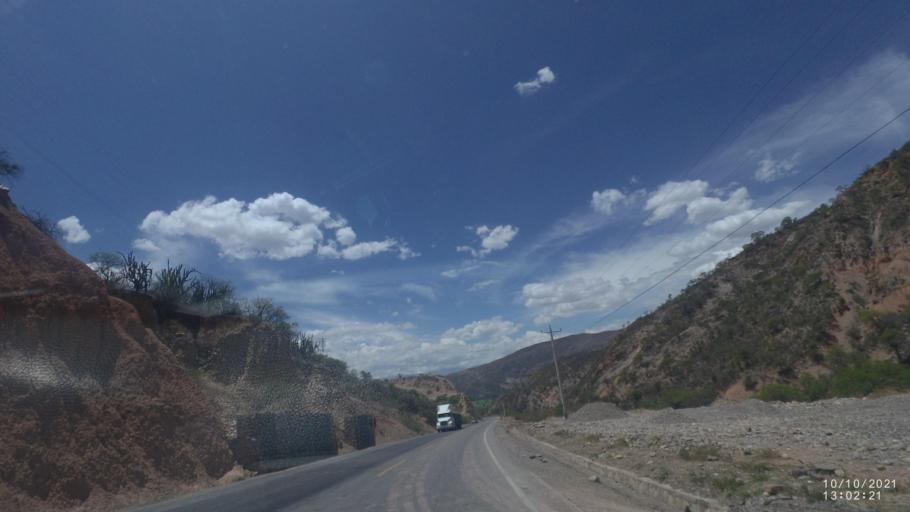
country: BO
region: Cochabamba
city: Sipe Sipe
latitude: -17.5841
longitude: -66.3542
